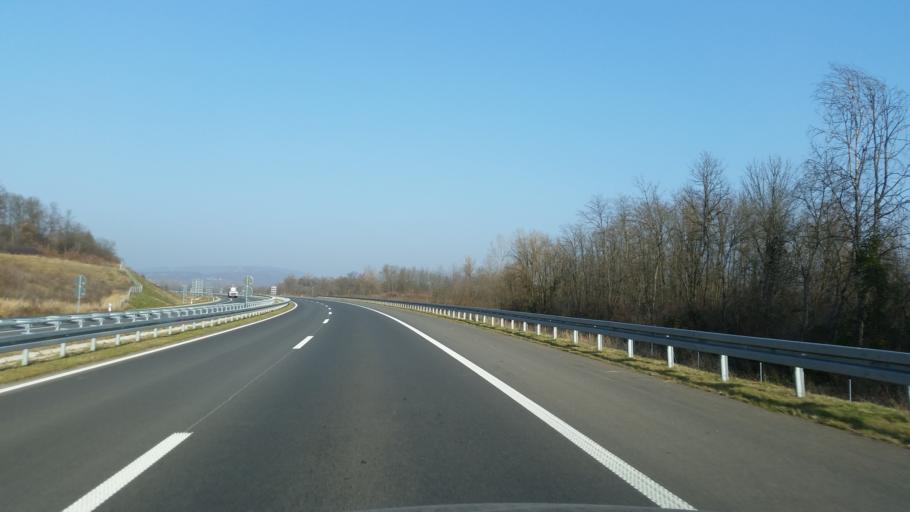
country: RS
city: Prislonica
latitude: 43.9262
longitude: 20.4012
